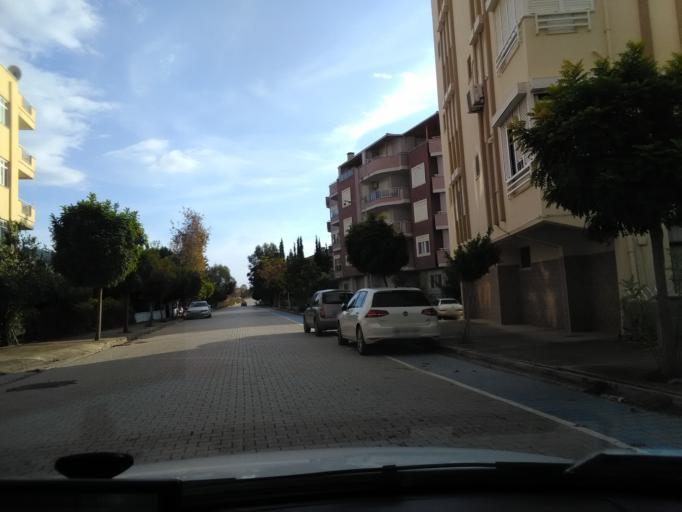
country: TR
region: Antalya
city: Gazipasa
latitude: 36.2645
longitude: 32.2888
